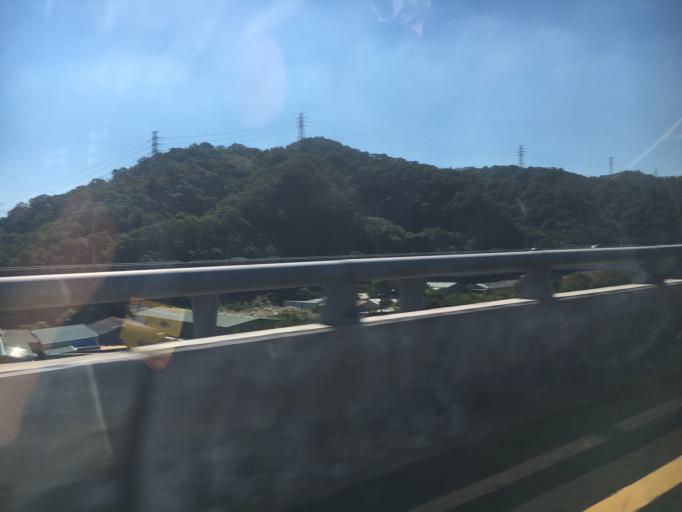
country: TW
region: Taipei
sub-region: Taipei
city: Banqiao
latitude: 25.0642
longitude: 121.4192
